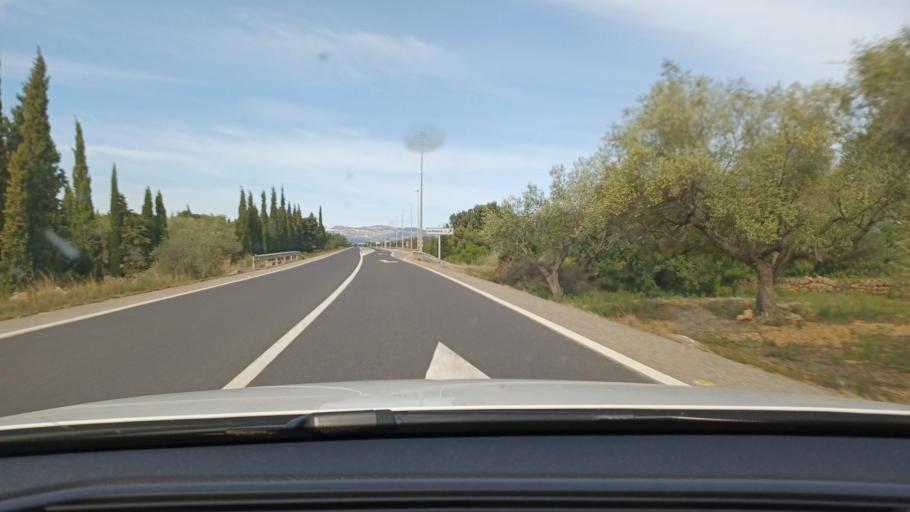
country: ES
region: Catalonia
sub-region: Provincia de Tarragona
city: Mas de Barberans
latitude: 40.6395
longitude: 0.3408
